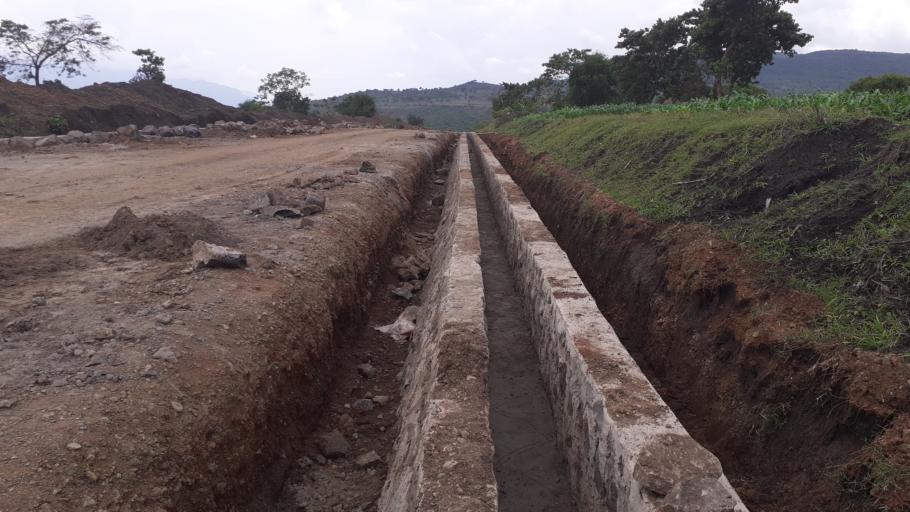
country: ET
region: Southern Nations, Nationalities, and People's Region
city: Areka
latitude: 7.5547
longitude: 37.5018
